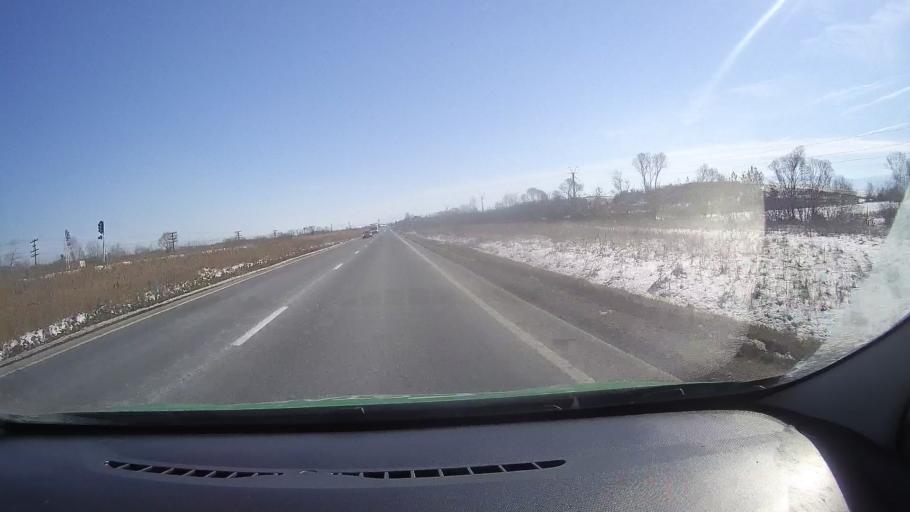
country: RO
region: Brasov
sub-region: Comuna Mandra
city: Mandra
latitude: 45.8294
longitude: 25.0240
